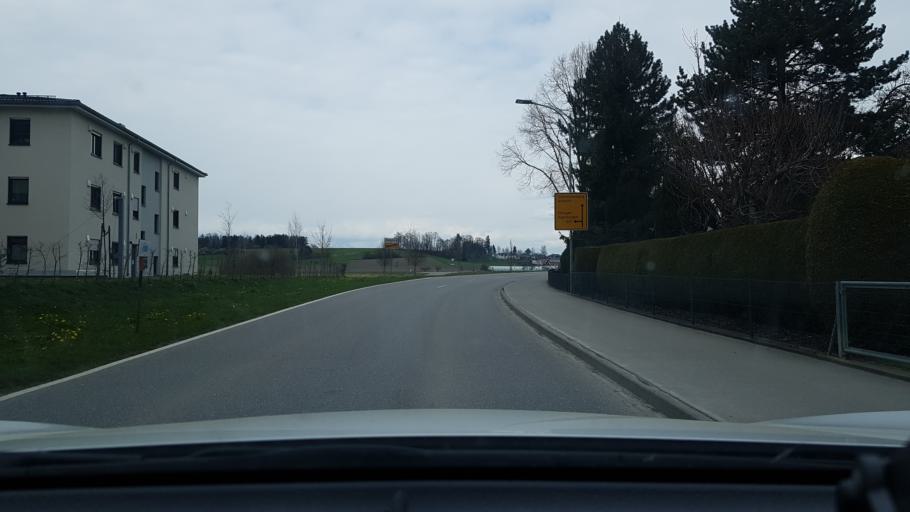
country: DE
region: Baden-Wuerttemberg
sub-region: Tuebingen Region
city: Warthausen
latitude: 48.1773
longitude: 9.7909
